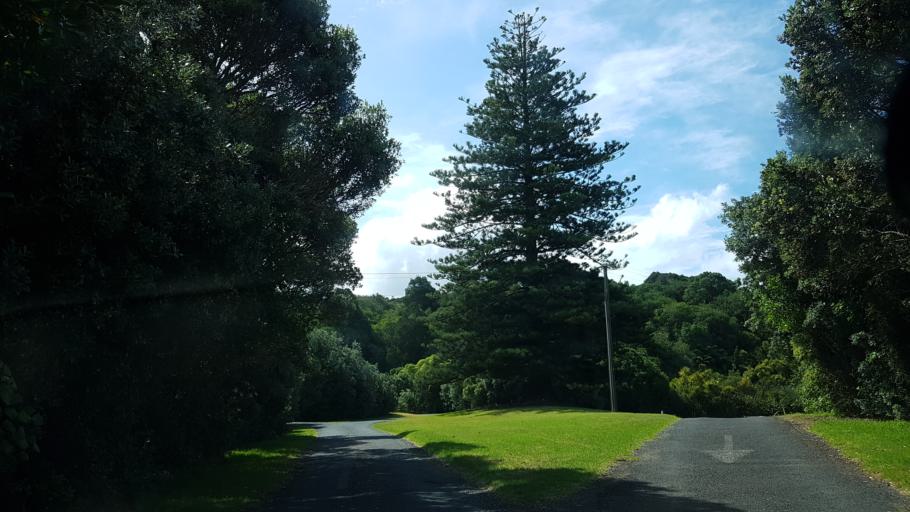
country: NZ
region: Auckland
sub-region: Auckland
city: Rothesay Bay
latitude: -36.6815
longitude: 174.7462
